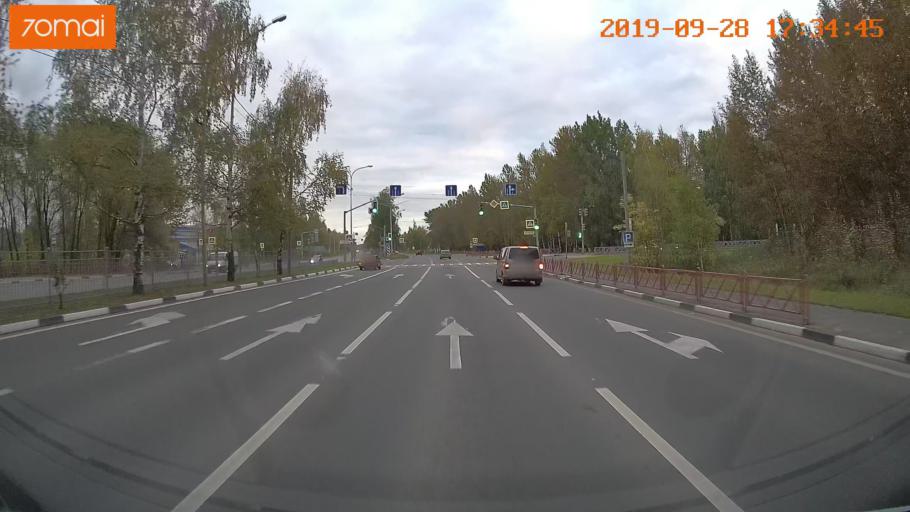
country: RU
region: Jaroslavl
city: Yaroslavl
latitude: 57.5558
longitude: 39.9412
